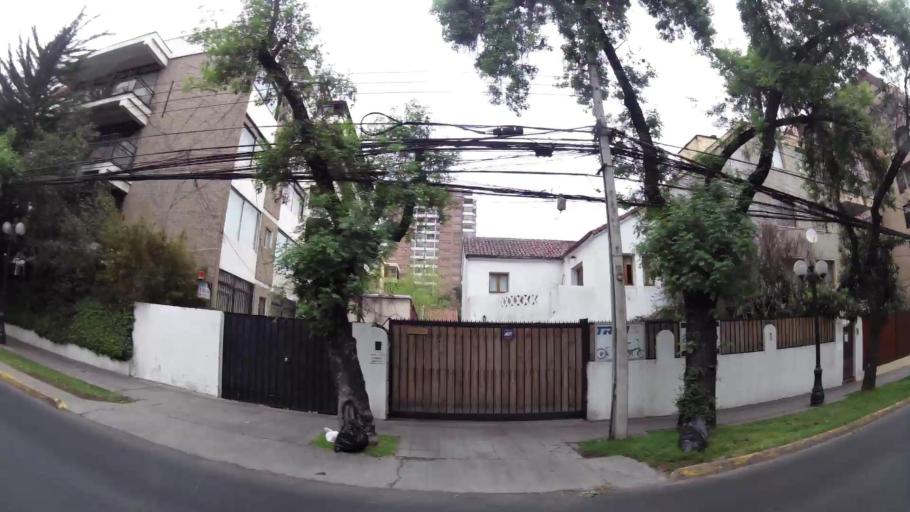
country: CL
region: Santiago Metropolitan
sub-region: Provincia de Santiago
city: Villa Presidente Frei, Nunoa, Santiago, Chile
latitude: -33.4282
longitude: -70.6080
